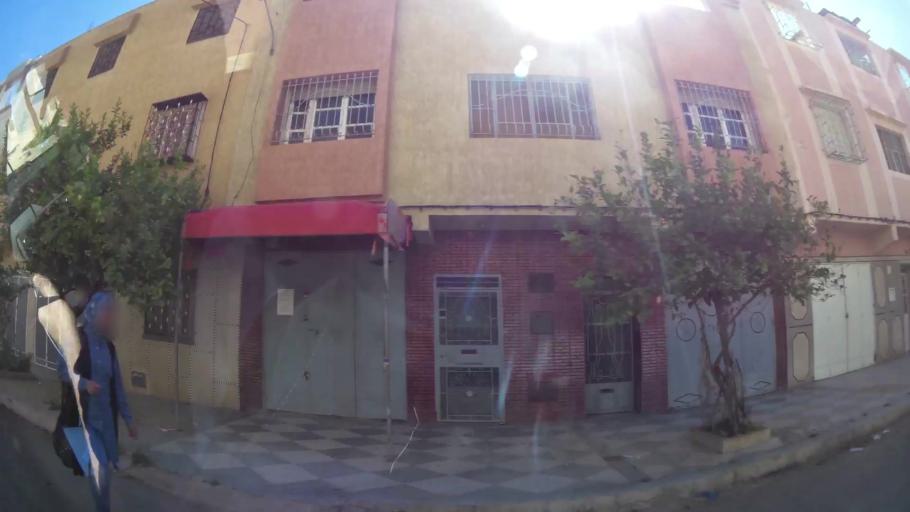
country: MA
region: Oriental
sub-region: Oujda-Angad
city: Oujda
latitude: 34.6681
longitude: -1.9281
